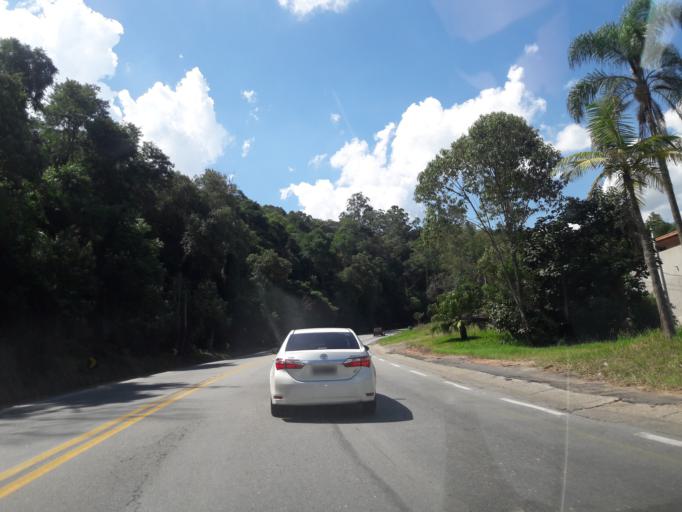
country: BR
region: Sao Paulo
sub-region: Francisco Morato
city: Francisco Morato
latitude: -23.2665
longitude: -46.7977
